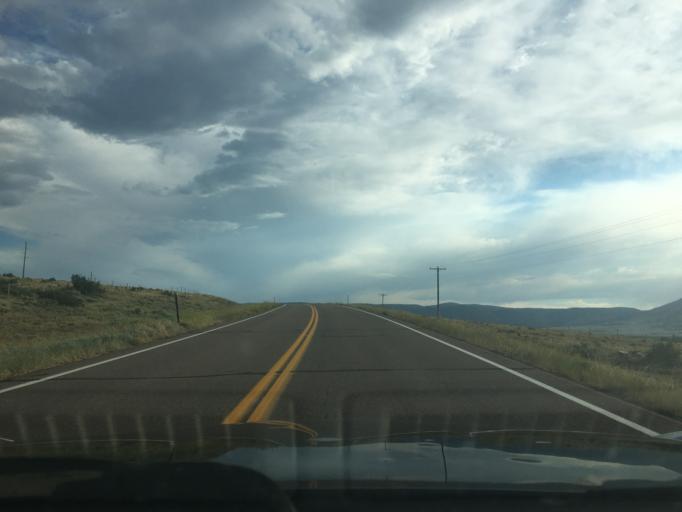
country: US
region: Wyoming
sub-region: Albany County
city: Laramie
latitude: 41.2784
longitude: -106.0660
